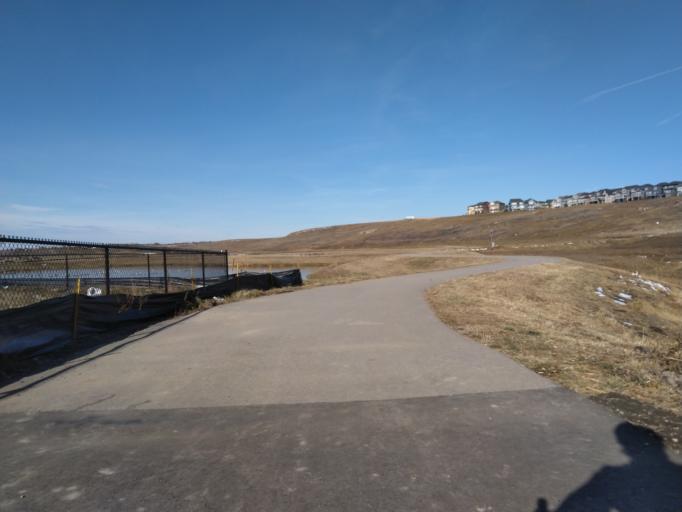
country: CA
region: Alberta
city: Calgary
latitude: 51.1778
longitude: -114.1299
